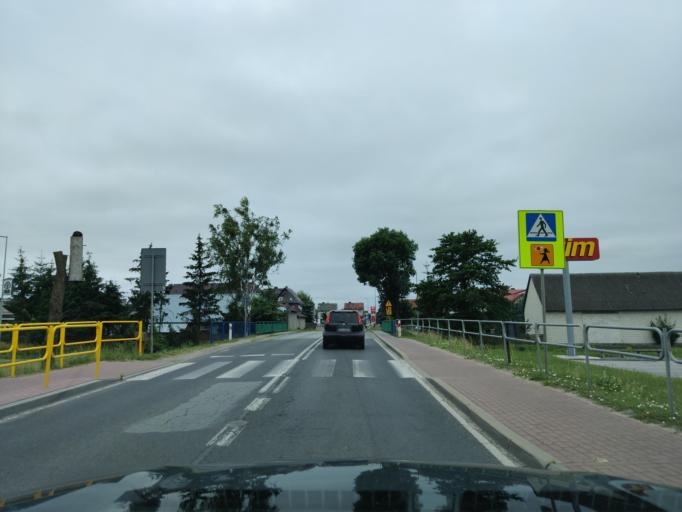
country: PL
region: Masovian Voivodeship
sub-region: Powiat ostrolecki
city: Myszyniec
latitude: 53.3870
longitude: 21.3409
